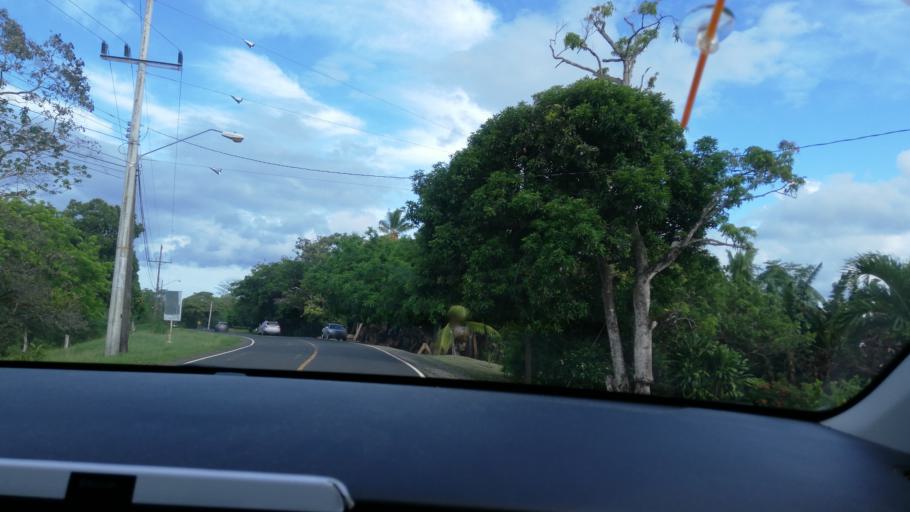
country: PA
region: Panama
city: Las Colinas
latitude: 8.4933
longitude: -80.0254
